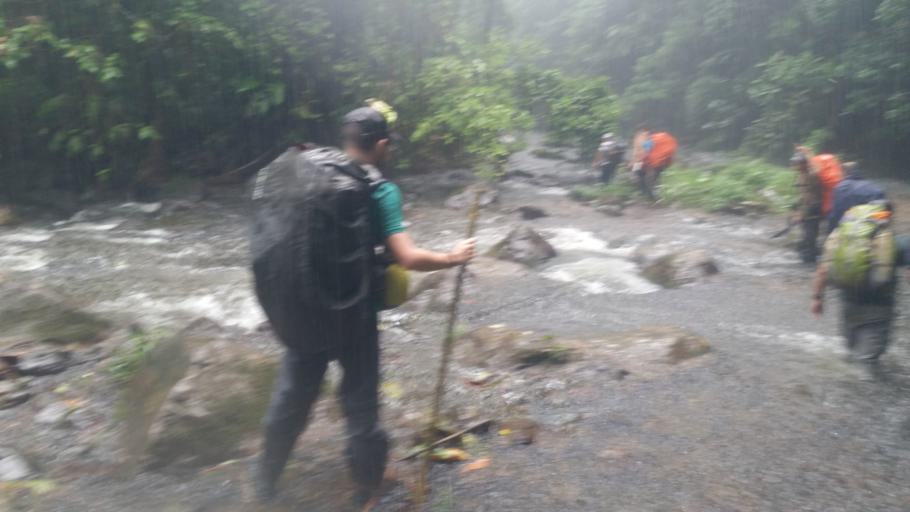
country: NI
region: Atlantico Norte (RAAN)
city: Bonanza
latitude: 14.0249
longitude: -84.7537
